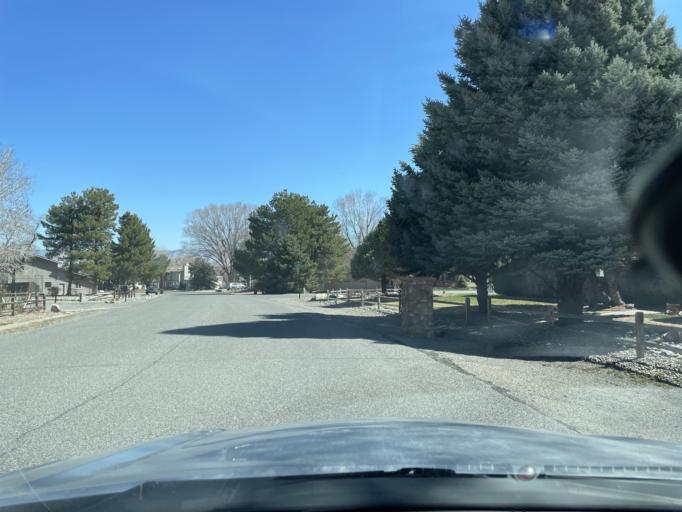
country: US
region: Colorado
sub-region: Mesa County
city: Redlands
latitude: 39.0806
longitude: -108.6731
